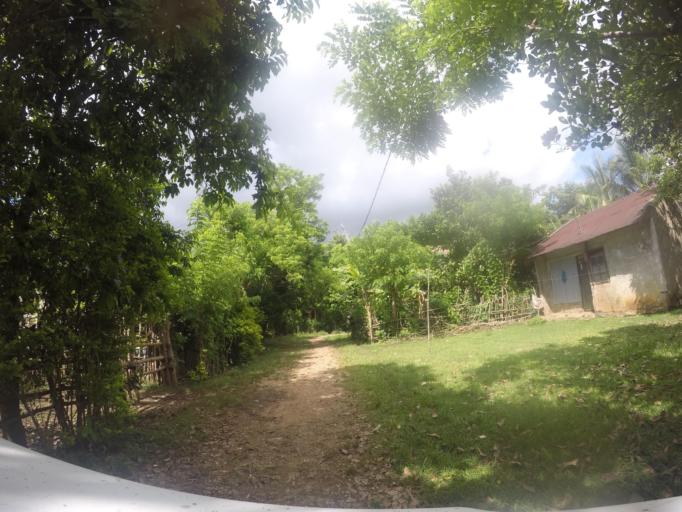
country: TL
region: Lautem
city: Lospalos
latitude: -8.5024
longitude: 127.0083
